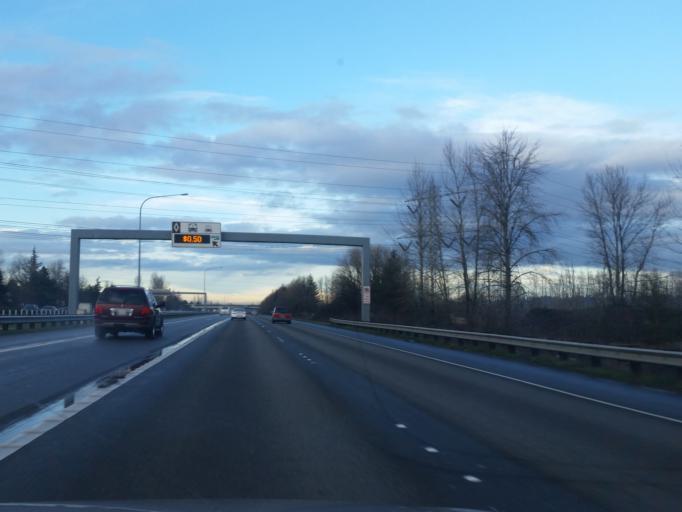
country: US
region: Washington
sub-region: King County
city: Auburn
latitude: 47.3337
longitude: -122.2447
